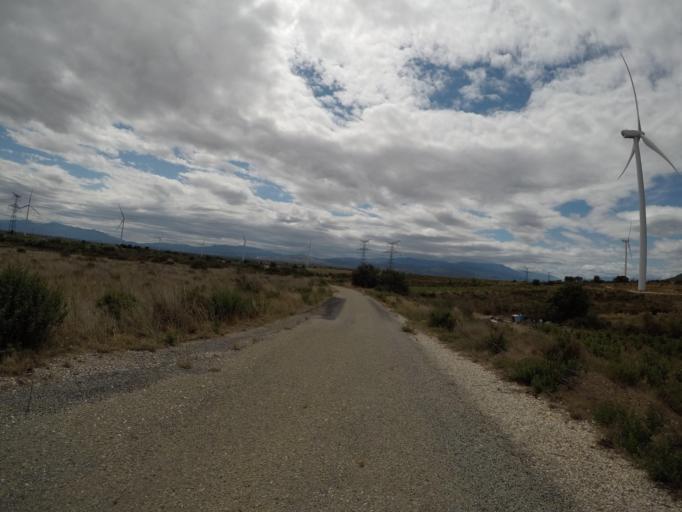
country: FR
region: Languedoc-Roussillon
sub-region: Departement des Pyrenees-Orientales
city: Corneilla-la-Riviere
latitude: 42.7232
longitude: 2.7458
